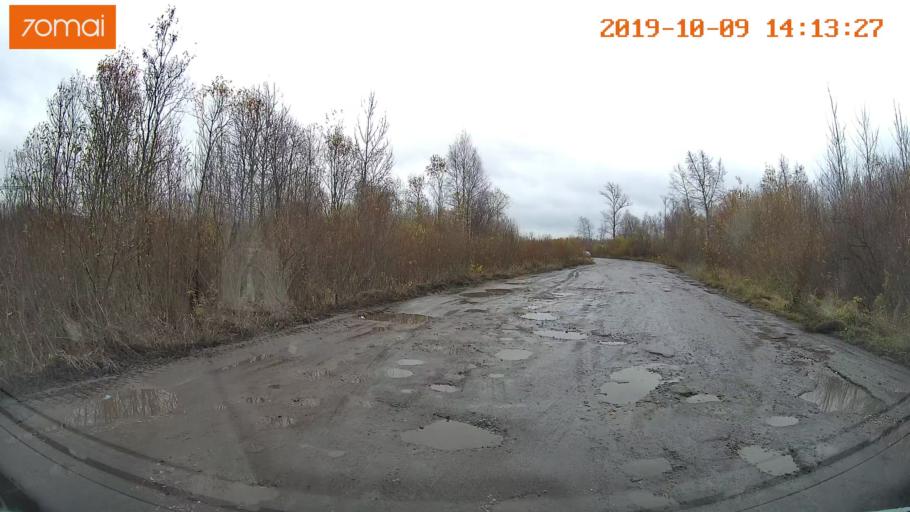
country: RU
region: Kostroma
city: Buy
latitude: 58.4812
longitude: 41.5115
